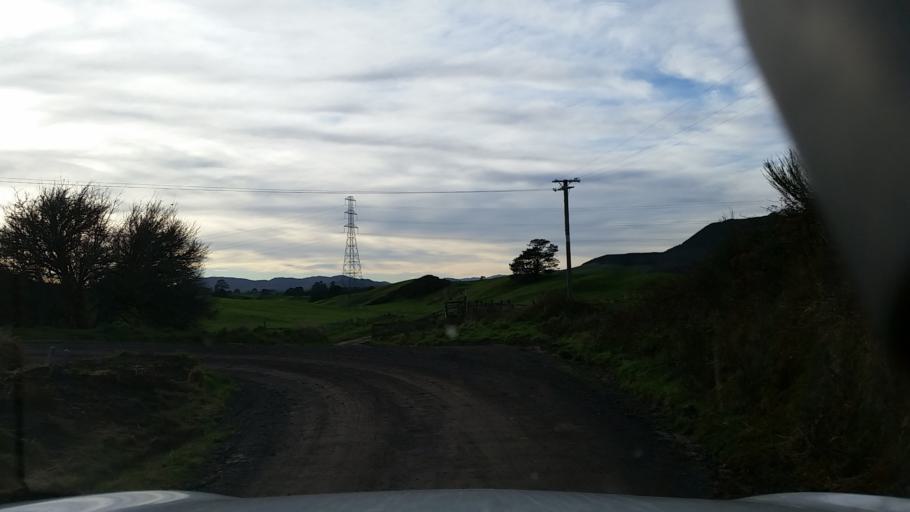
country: NZ
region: Bay of Plenty
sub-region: Rotorua District
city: Rotorua
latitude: -38.2275
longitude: 176.1624
